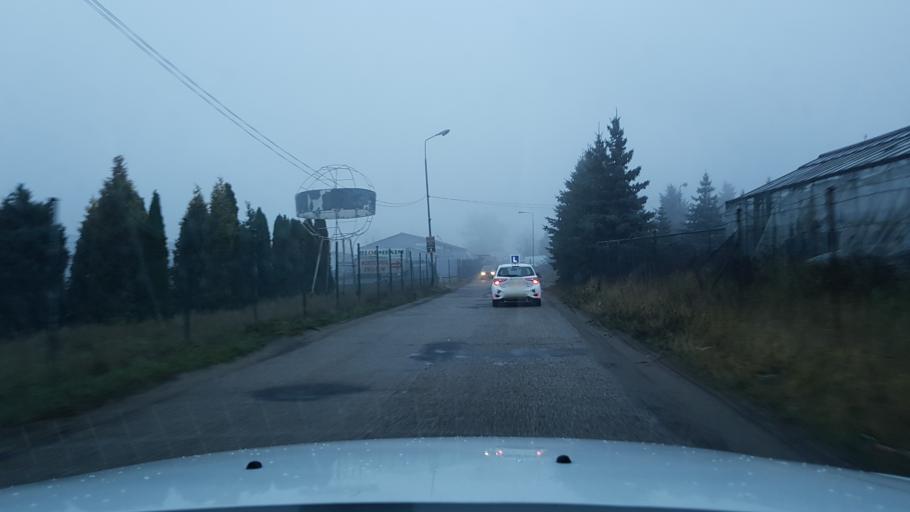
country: PL
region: West Pomeranian Voivodeship
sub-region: Powiat policki
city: Przeclaw
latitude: 53.3890
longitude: 14.4894
